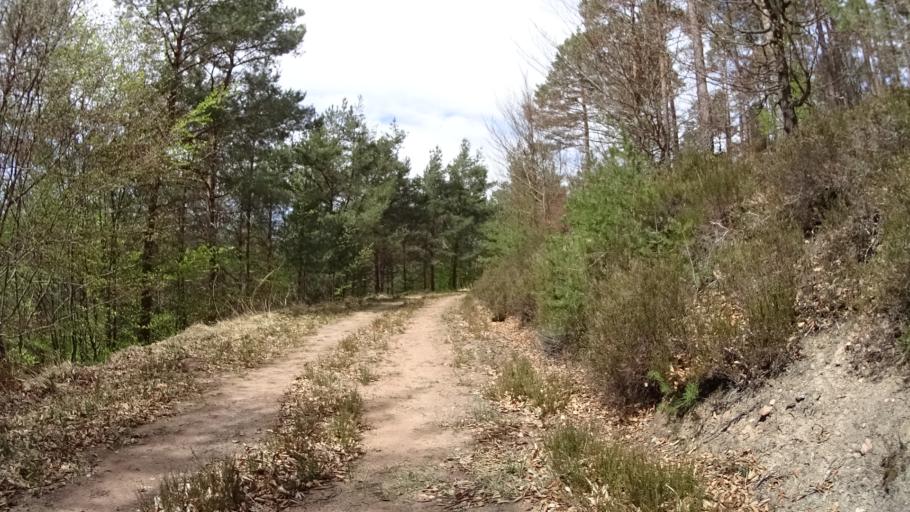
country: DE
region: Rheinland-Pfalz
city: Ramberg
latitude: 49.3194
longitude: 8.0018
